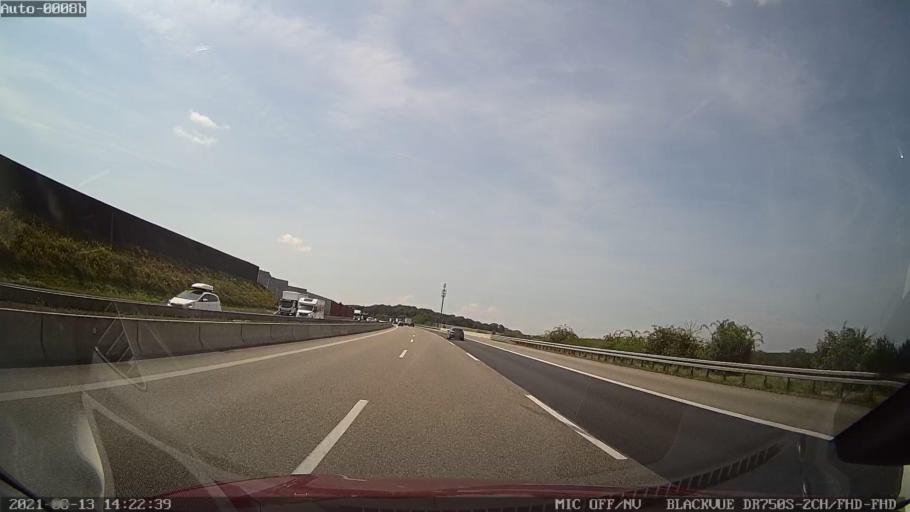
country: DE
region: Baden-Wuerttemberg
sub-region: Regierungsbezirk Stuttgart
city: Massenbachhausen
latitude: 49.2146
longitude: 9.0588
